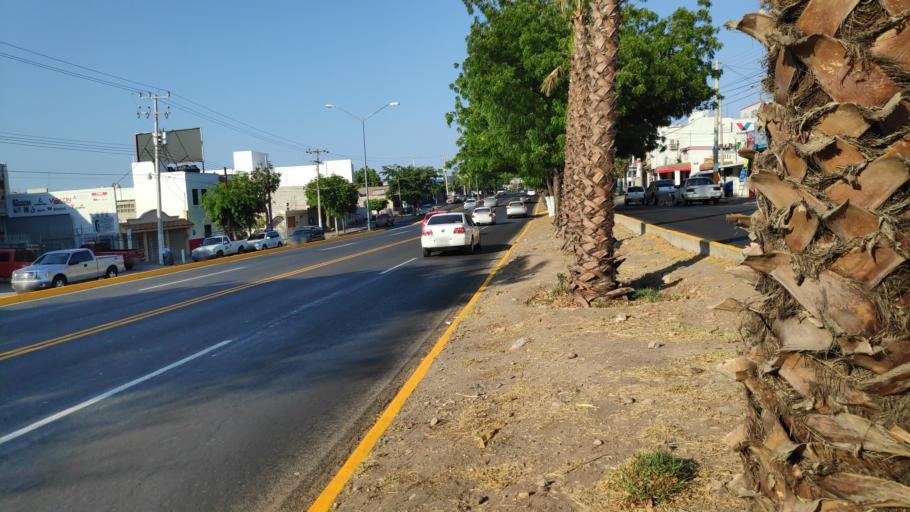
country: MX
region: Sinaloa
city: Culiacan
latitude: 24.7941
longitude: -107.4083
